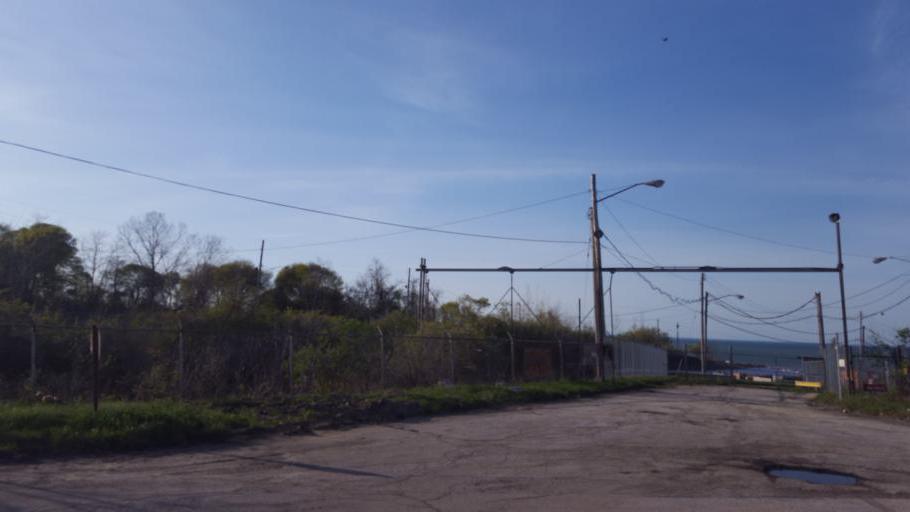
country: US
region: Ohio
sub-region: Ashtabula County
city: Edgewood
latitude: 41.9100
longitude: -80.7625
